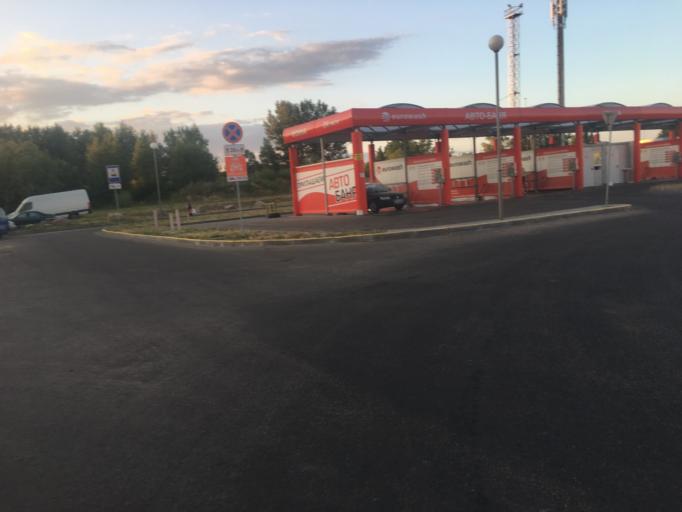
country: BY
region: Grodnenskaya
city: Hrodna
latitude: 53.7165
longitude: 23.8496
